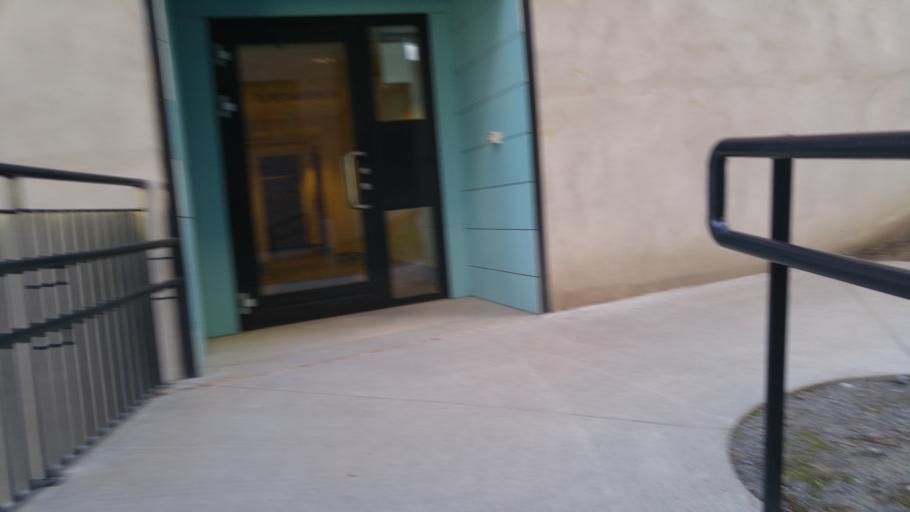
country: NO
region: Oslo
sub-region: Oslo
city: Oslo
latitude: 59.9031
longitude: 10.7872
